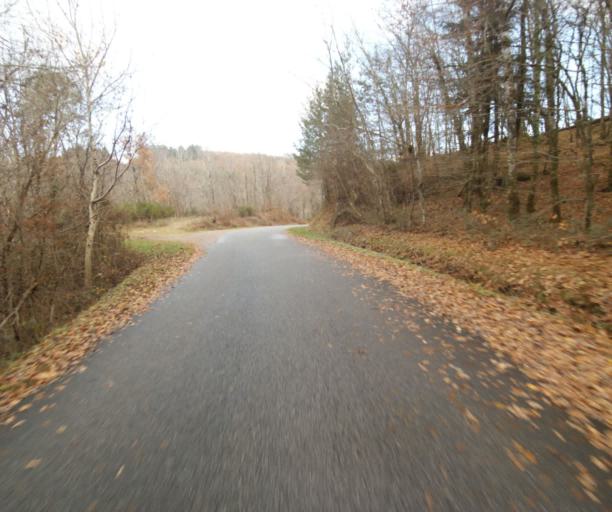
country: FR
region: Limousin
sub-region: Departement de la Correze
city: Laguenne
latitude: 45.2403
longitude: 1.7805
